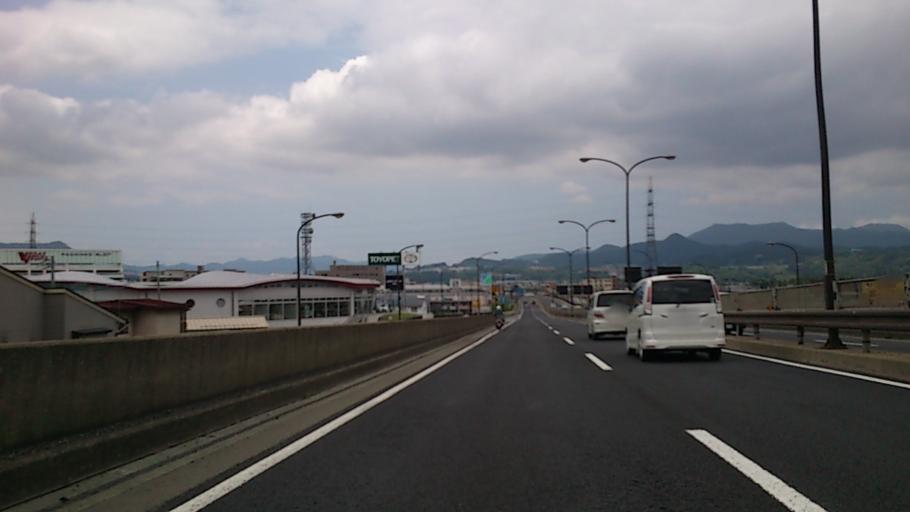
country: JP
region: Yamagata
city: Yamagata-shi
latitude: 38.2127
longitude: 140.3215
